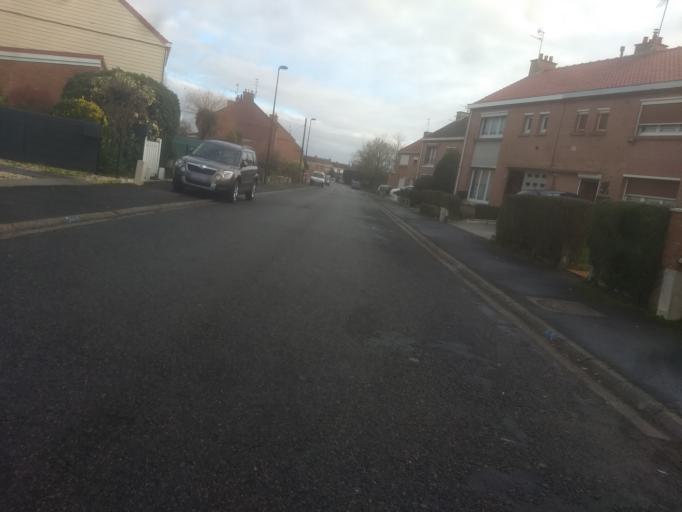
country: FR
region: Nord-Pas-de-Calais
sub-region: Departement du Pas-de-Calais
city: Dainville
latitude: 50.2874
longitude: 2.7345
